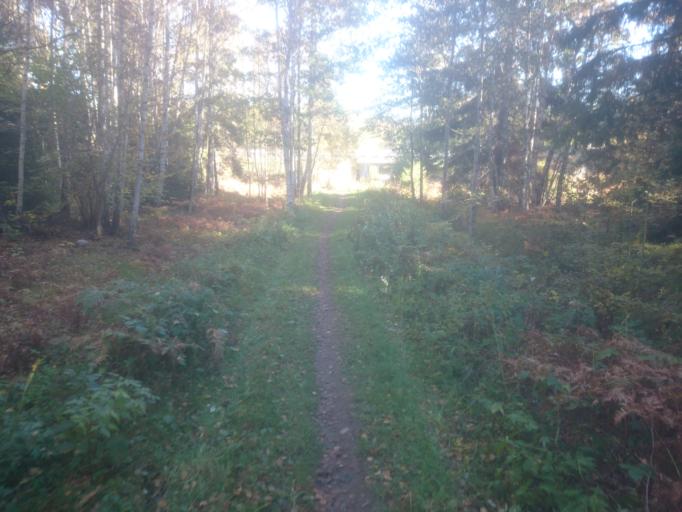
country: SE
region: Stockholm
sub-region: Upplands-Bro Kommun
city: Kungsaengen
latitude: 59.4984
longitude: 17.7400
